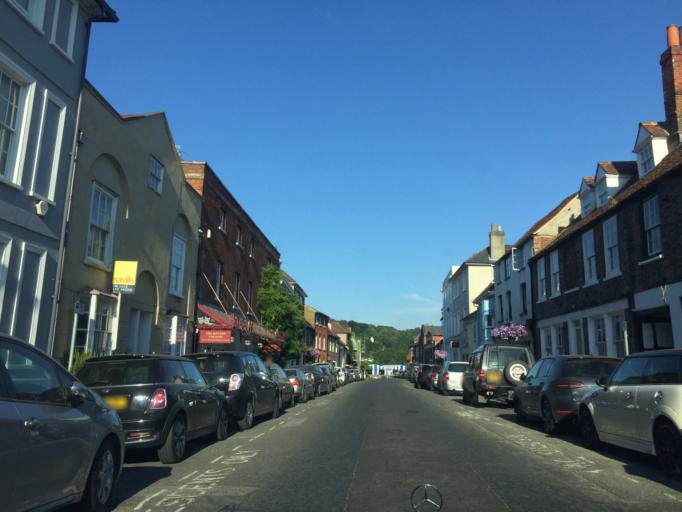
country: GB
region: England
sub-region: Oxfordshire
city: Henley on Thames
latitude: 51.5394
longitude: -0.9037
